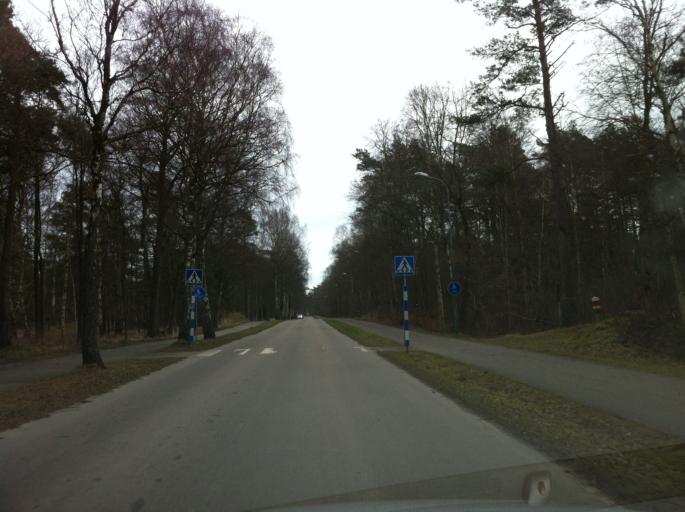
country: SE
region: Skane
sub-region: Angelholms Kommun
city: AEngelholm
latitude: 56.2536
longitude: 12.8391
